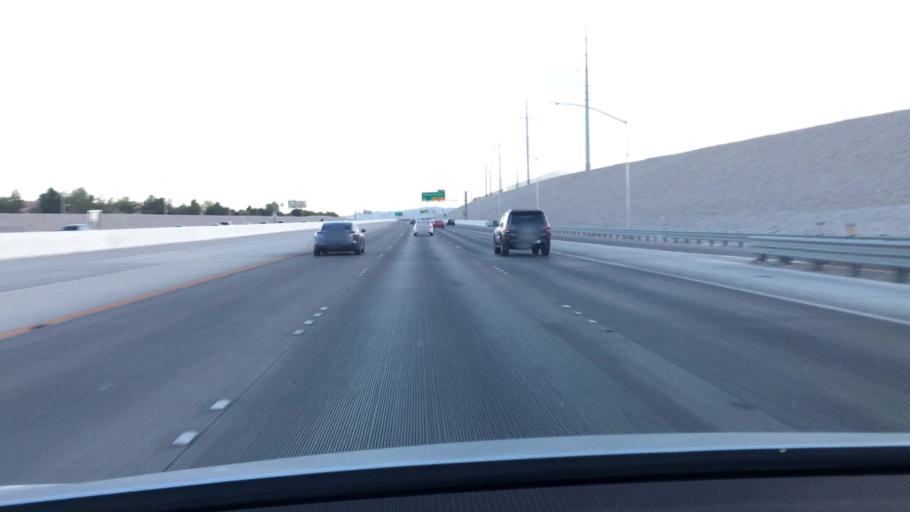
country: US
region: Nevada
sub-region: Clark County
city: Summerlin South
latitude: 36.2033
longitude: -115.3413
